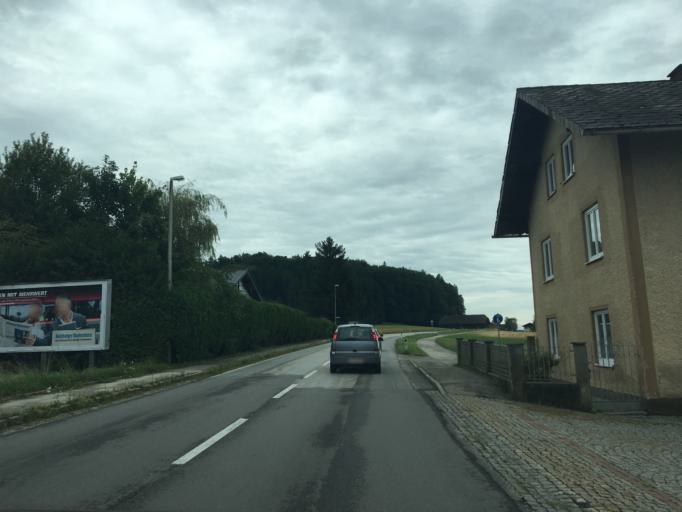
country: AT
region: Salzburg
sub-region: Politischer Bezirk Salzburg-Umgebung
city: Dorfbeuern
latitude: 48.0510
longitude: 12.9857
